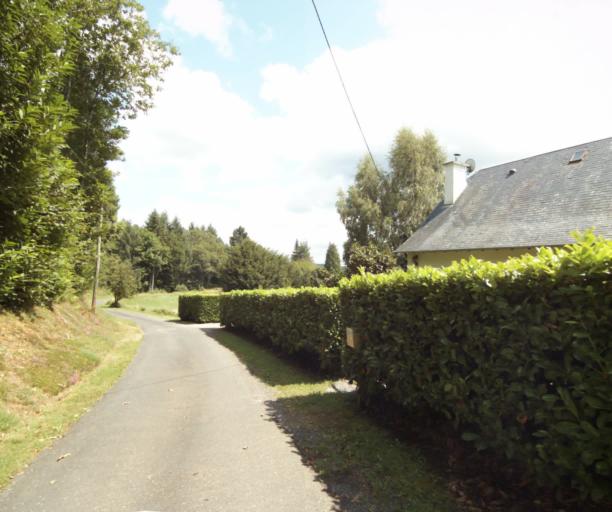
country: FR
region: Limousin
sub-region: Departement de la Correze
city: Sainte-Fortunade
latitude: 45.1975
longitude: 1.8402
